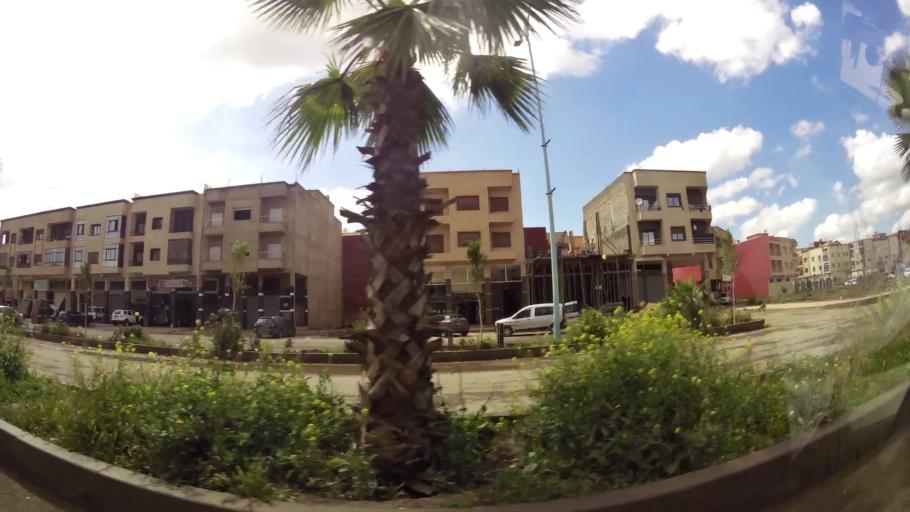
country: MA
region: Grand Casablanca
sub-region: Mediouna
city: Mediouna
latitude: 33.3813
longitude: -7.5345
